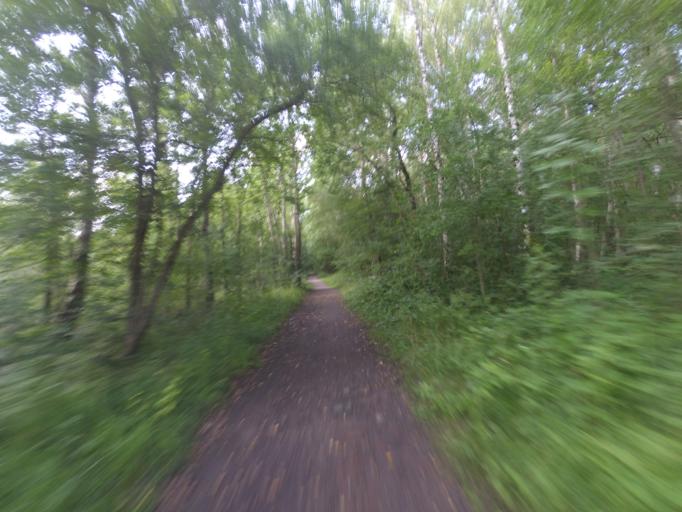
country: DE
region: Schleswig-Holstein
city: Glinde
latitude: 53.5022
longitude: 10.1820
